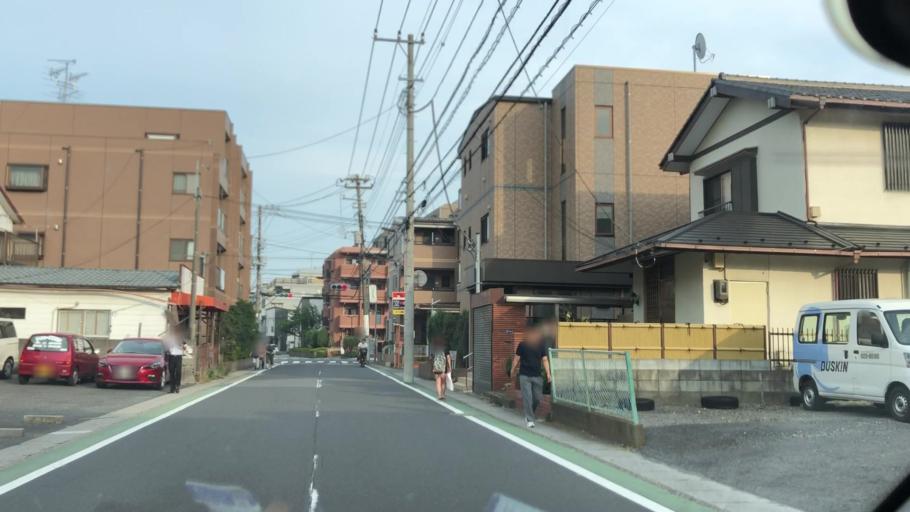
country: JP
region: Tokyo
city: Urayasu
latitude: 35.6706
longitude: 139.9049
